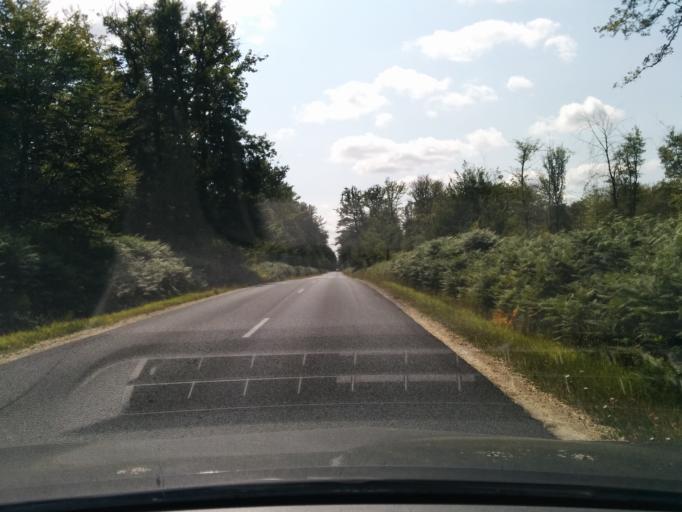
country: FR
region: Centre
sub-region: Departement du Cher
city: Vierzon
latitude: 47.2566
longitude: 2.1334
